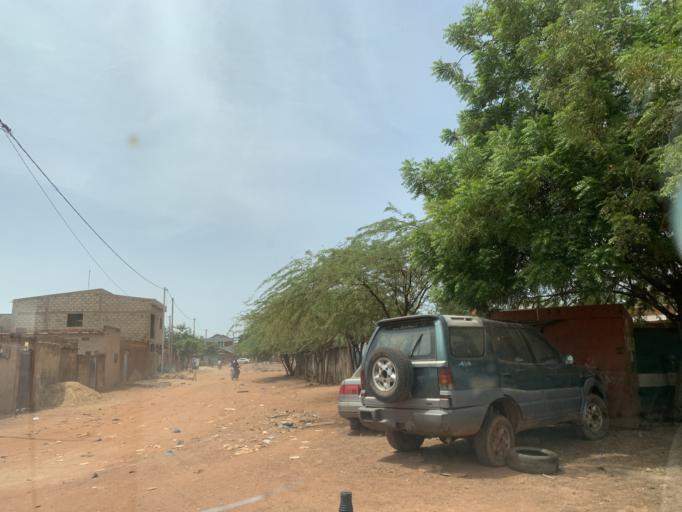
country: BF
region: Centre
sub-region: Kadiogo Province
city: Ouagadougou
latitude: 12.3278
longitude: -1.4872
